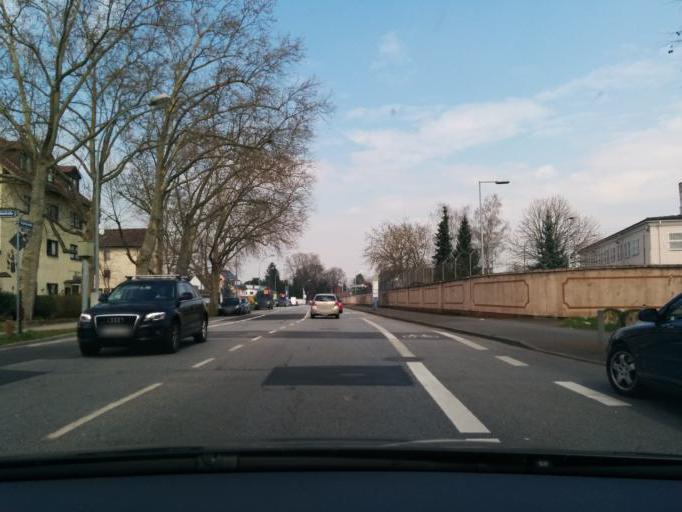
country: DE
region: Rheinland-Pfalz
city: Mainz
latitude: 50.0125
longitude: 8.2822
